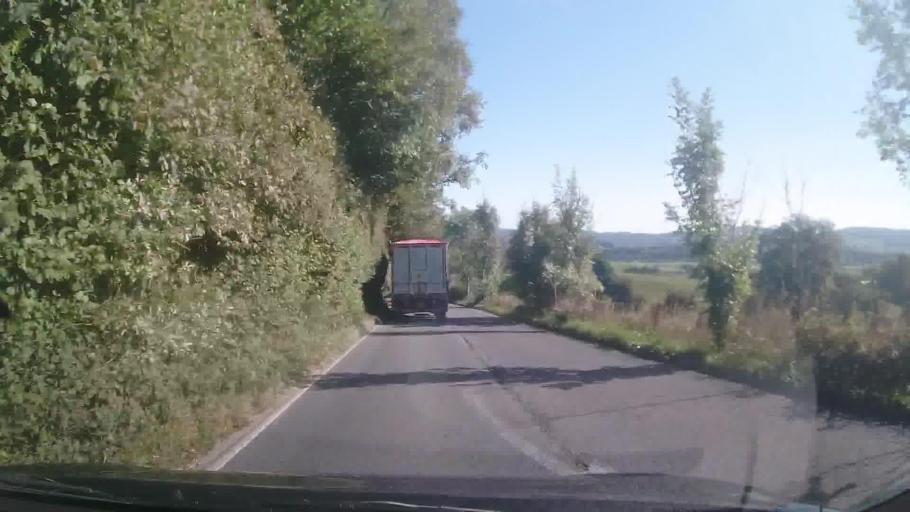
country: GB
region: England
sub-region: Cumbria
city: Millom
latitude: 54.2713
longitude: -3.2417
